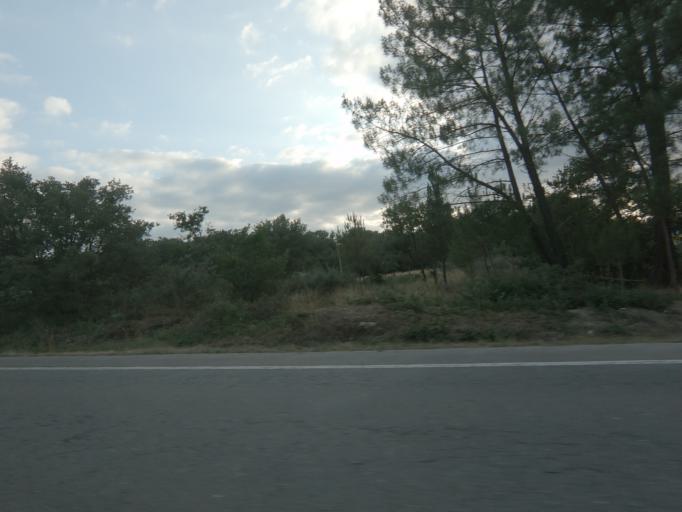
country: ES
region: Galicia
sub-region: Provincia de Ourense
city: Taboadela
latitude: 42.2770
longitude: -7.8363
